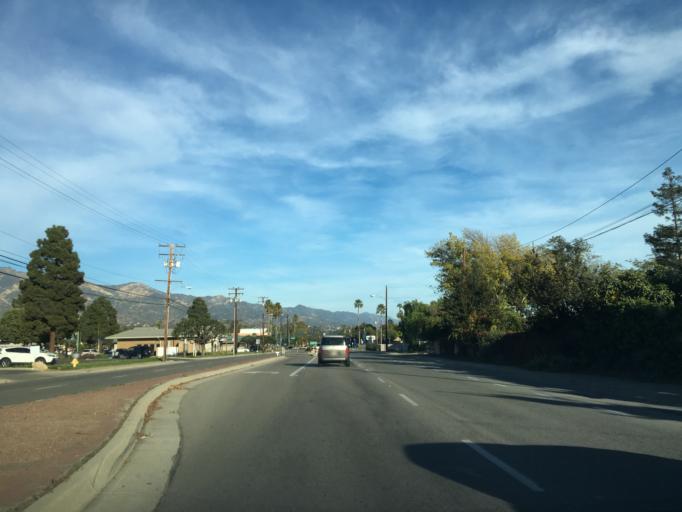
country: US
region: California
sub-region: Santa Barbara County
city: Goleta
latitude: 34.4360
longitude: -119.7927
